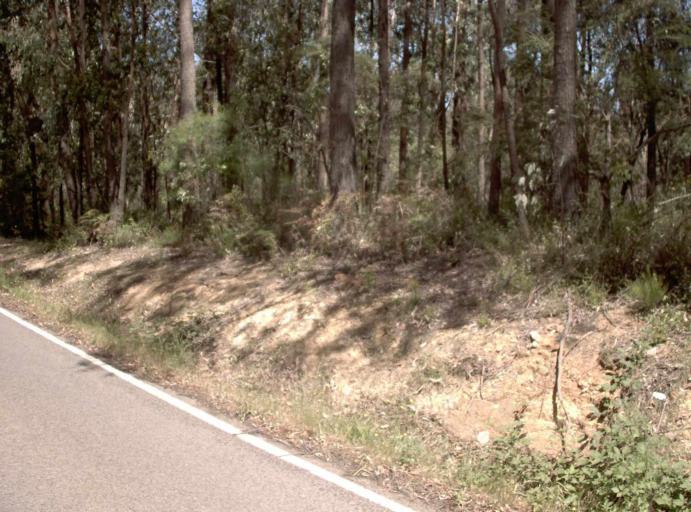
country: AU
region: Victoria
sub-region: Baw Baw
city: Warragul
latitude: -37.8860
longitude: 146.0581
